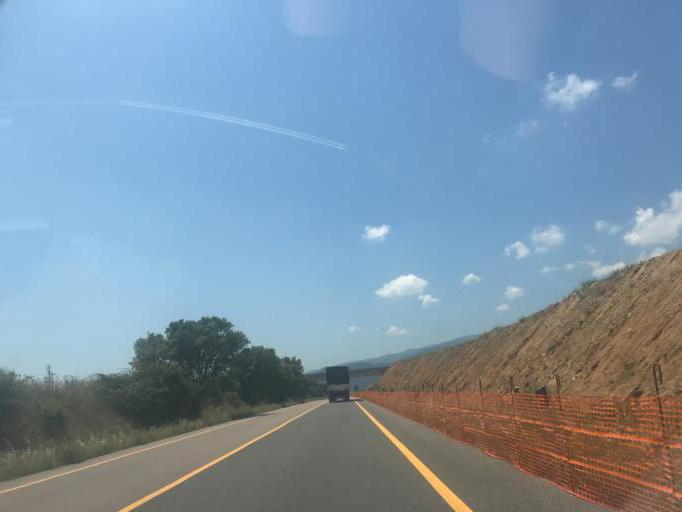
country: IT
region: Sardinia
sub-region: Provincia di Olbia-Tempio
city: Berchidda
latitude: 40.7797
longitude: 9.2295
